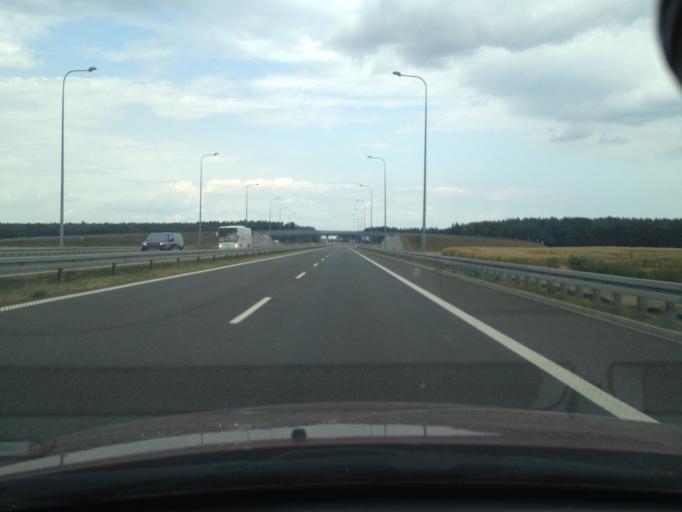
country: PL
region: West Pomeranian Voivodeship
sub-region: Powiat pyrzycki
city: Bielice
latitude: 53.1460
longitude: 14.7165
